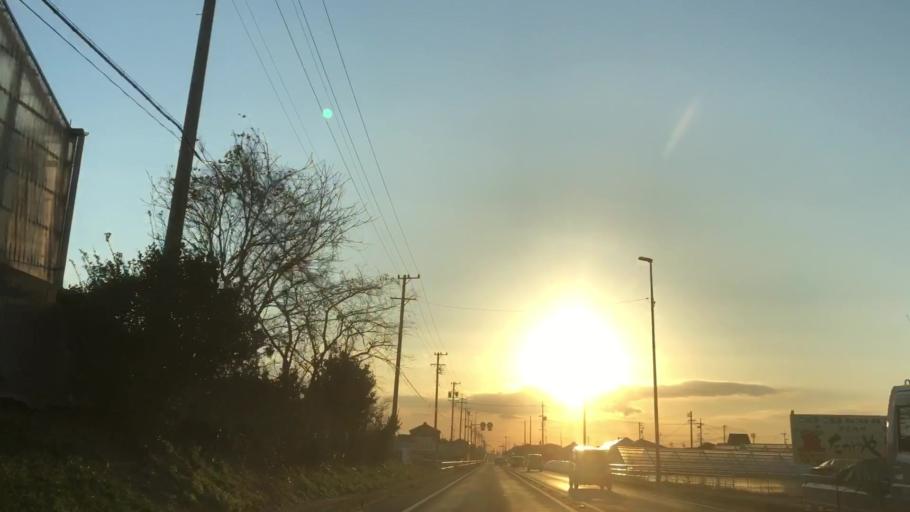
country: JP
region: Aichi
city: Tahara
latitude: 34.6347
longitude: 137.1260
